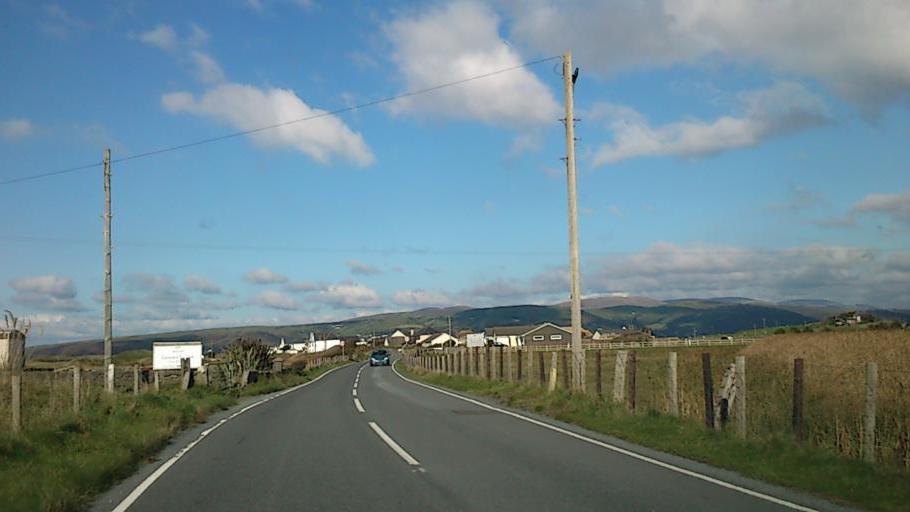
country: GB
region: Wales
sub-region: County of Ceredigion
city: Bow Street
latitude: 52.5089
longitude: -4.0533
